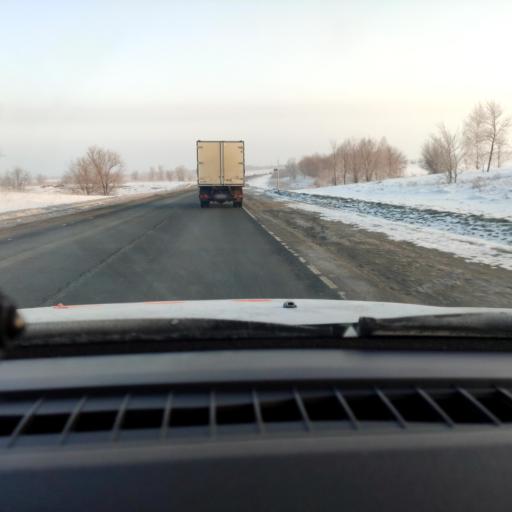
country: RU
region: Samara
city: Chapayevsk
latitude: 53.0063
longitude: 49.7698
